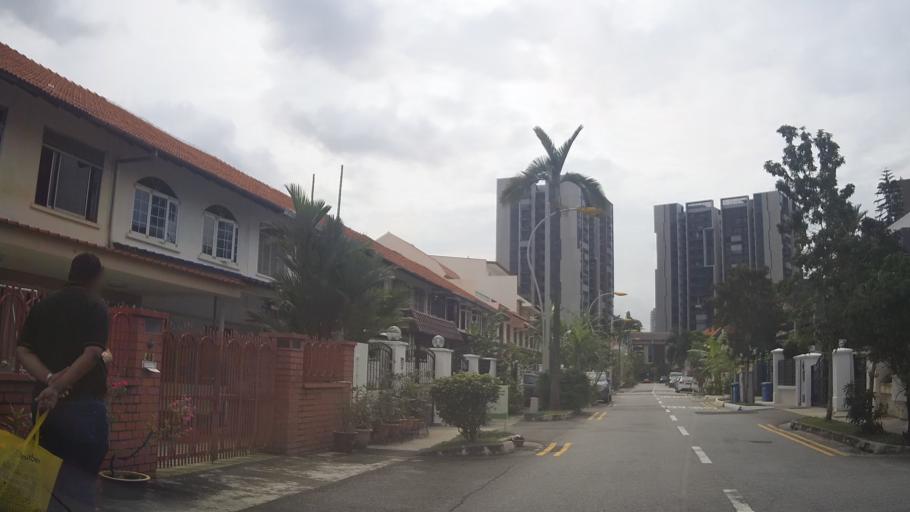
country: SG
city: Singapore
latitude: 1.3294
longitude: 103.8715
